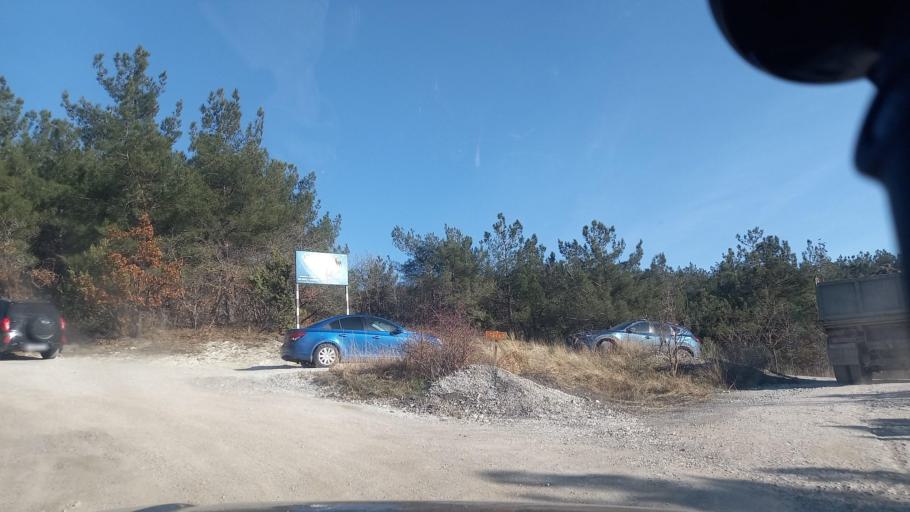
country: RU
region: Krasnodarskiy
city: Kabardinka
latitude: 44.6287
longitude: 37.9156
